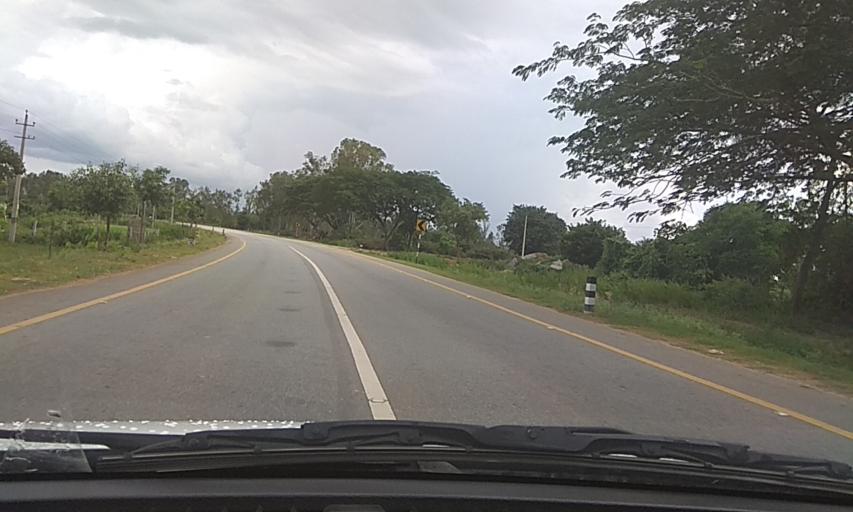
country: IN
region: Karnataka
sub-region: Tumkur
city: Kunigal
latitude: 12.9150
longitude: 77.0321
